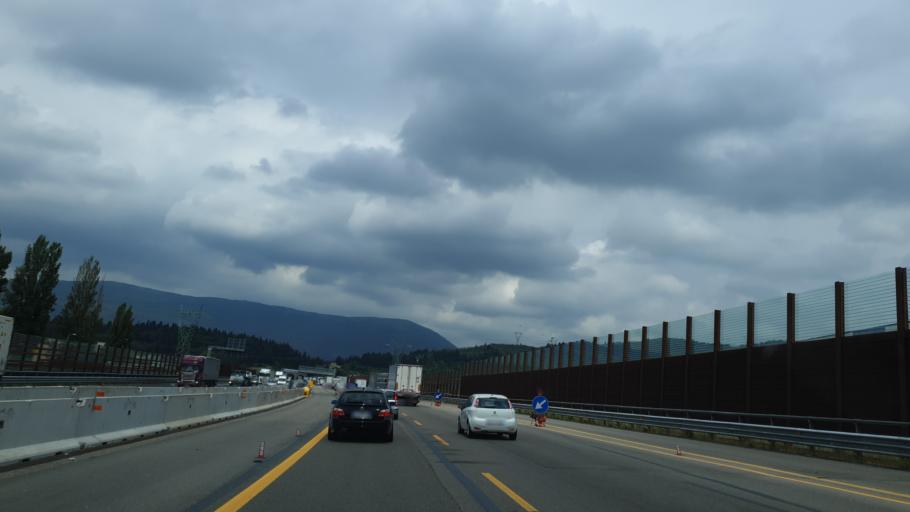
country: IT
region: Tuscany
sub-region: Province of Florence
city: Calenzano
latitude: 43.8606
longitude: 11.1776
